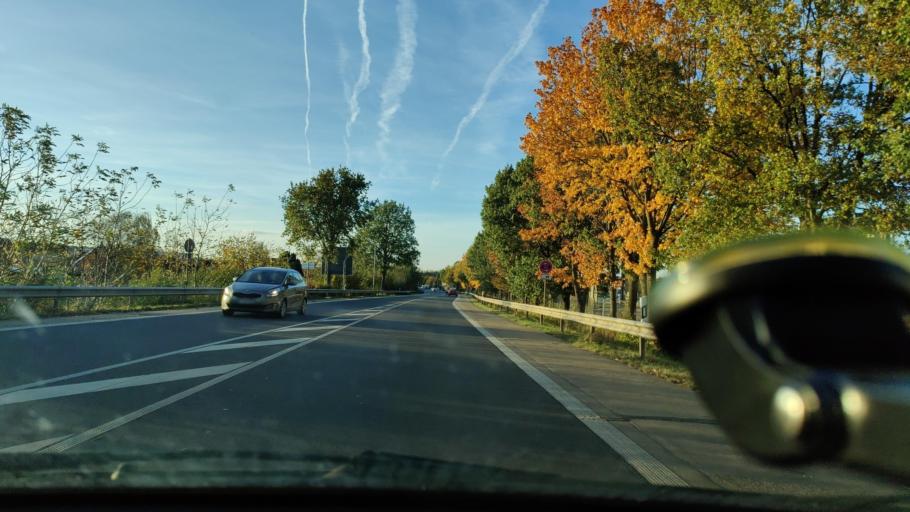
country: DE
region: North Rhine-Westphalia
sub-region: Regierungsbezirk Dusseldorf
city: Korschenbroich
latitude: 51.2242
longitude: 6.4807
